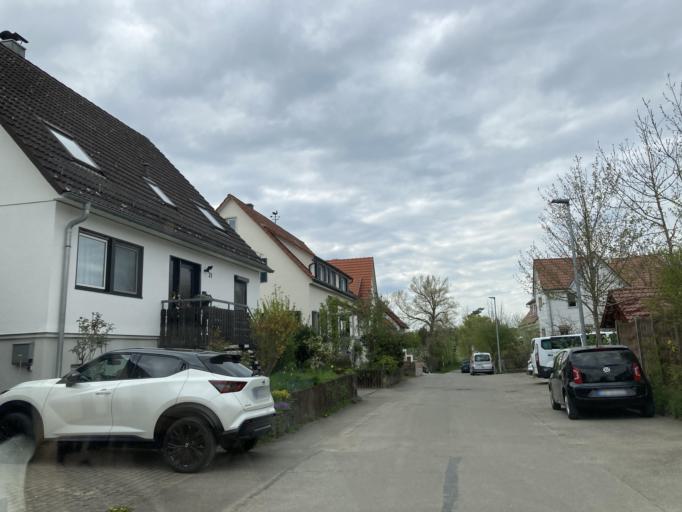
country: DE
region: Baden-Wuerttemberg
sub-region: Tuebingen Region
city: Kusterdingen
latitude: 48.5040
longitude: 9.1287
